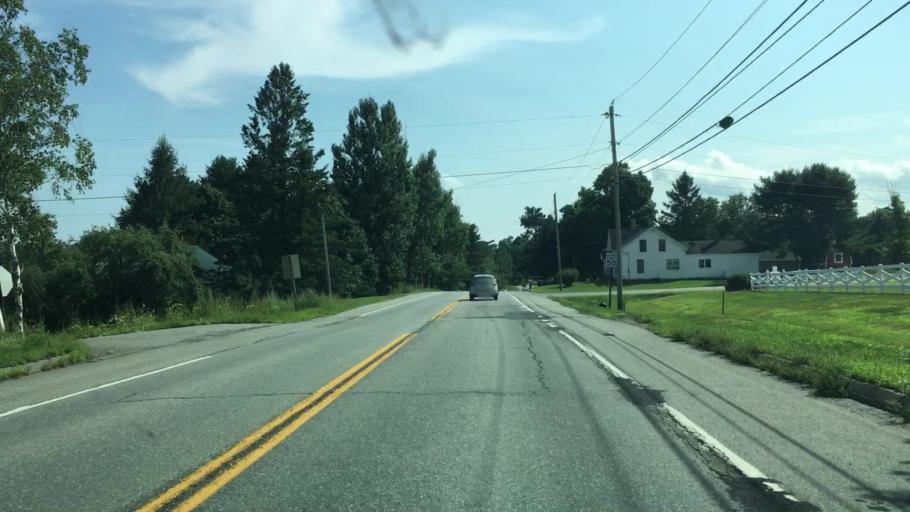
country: US
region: Maine
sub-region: Penobscot County
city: Orrington
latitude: 44.7150
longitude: -68.8462
